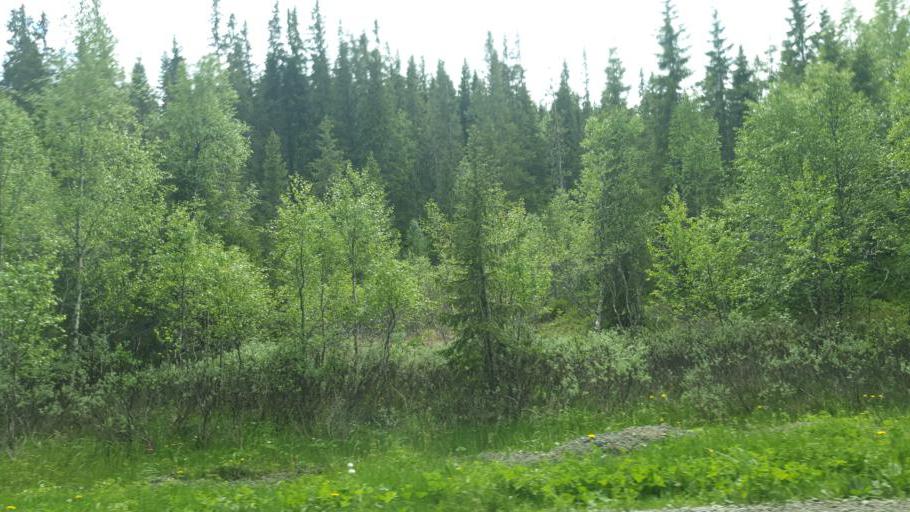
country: NO
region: Nord-Trondelag
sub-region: Leksvik
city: Leksvik
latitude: 63.6937
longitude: 10.4442
